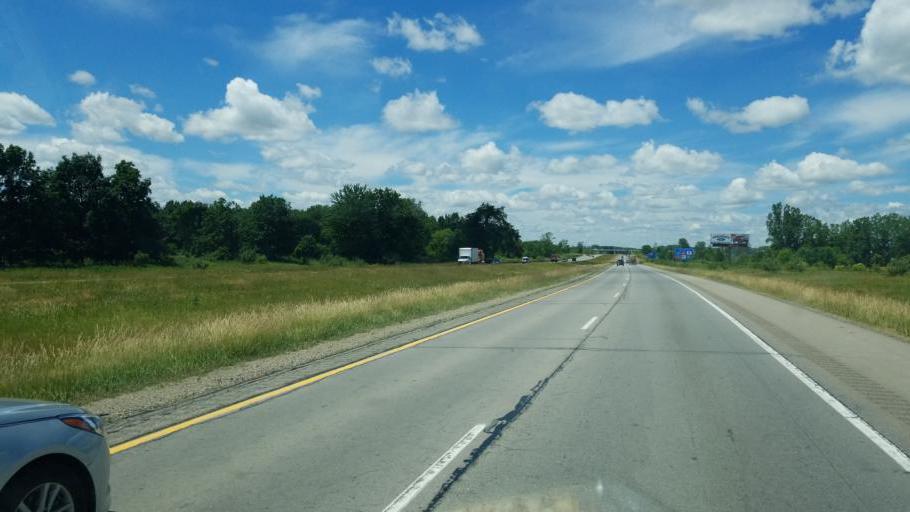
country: US
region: Michigan
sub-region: Livingston County
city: Fowlerville
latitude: 42.6473
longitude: -84.0589
